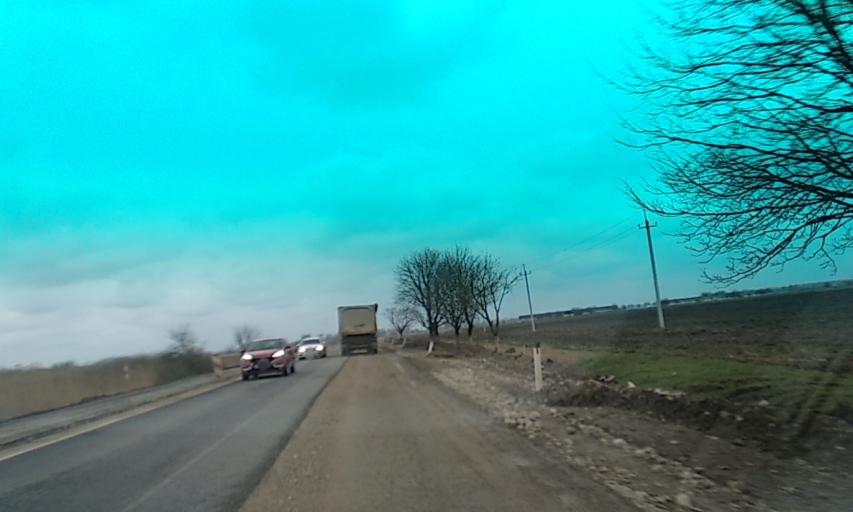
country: RU
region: Krasnodarskiy
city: Velikovechnoye
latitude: 44.9930
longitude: 39.7131
